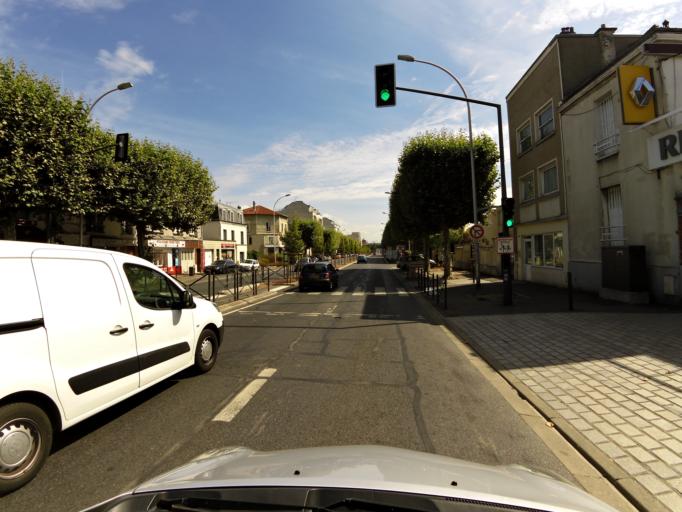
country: FR
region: Ile-de-France
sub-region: Departement du Val-de-Marne
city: Le Perreux-sur-Marne
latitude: 48.8517
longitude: 2.5081
